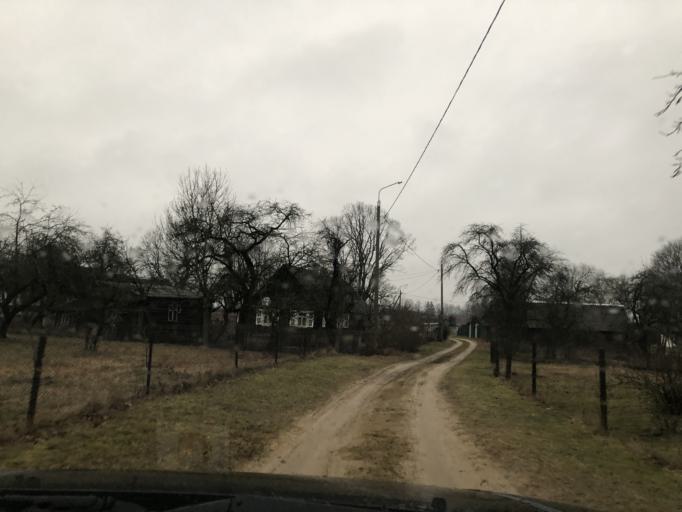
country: LT
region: Alytaus apskritis
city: Druskininkai
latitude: 53.9099
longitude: 24.1776
